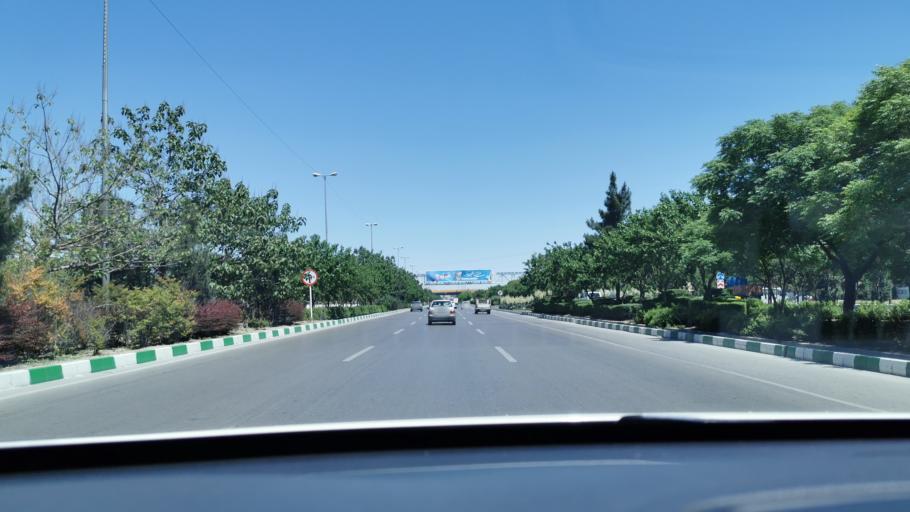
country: IR
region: Razavi Khorasan
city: Mashhad
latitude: 36.2582
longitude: 59.6295
